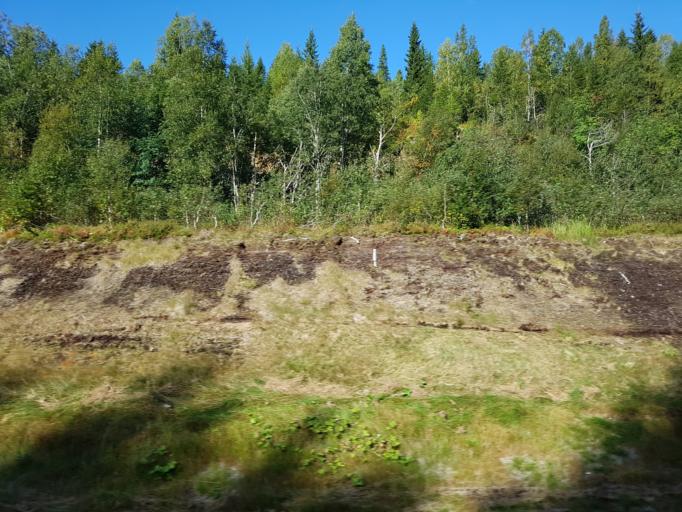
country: NO
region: Sor-Trondelag
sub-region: Trondheim
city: Trondheim
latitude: 63.6673
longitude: 10.2471
